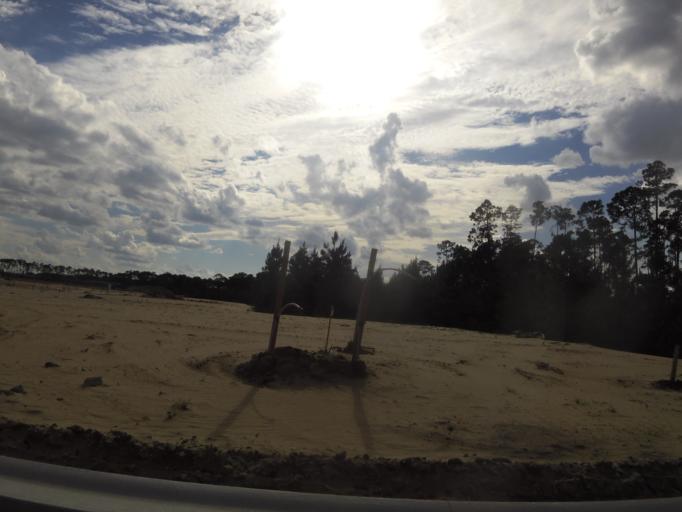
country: US
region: Florida
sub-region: Saint Johns County
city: Palm Valley
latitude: 30.1808
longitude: -81.5069
